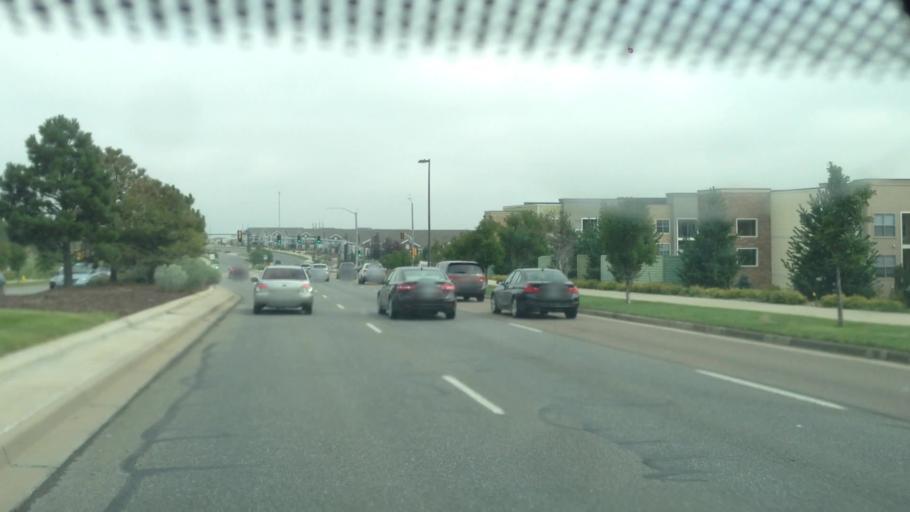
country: US
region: Colorado
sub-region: Douglas County
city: Parker
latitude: 39.6031
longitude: -104.7029
